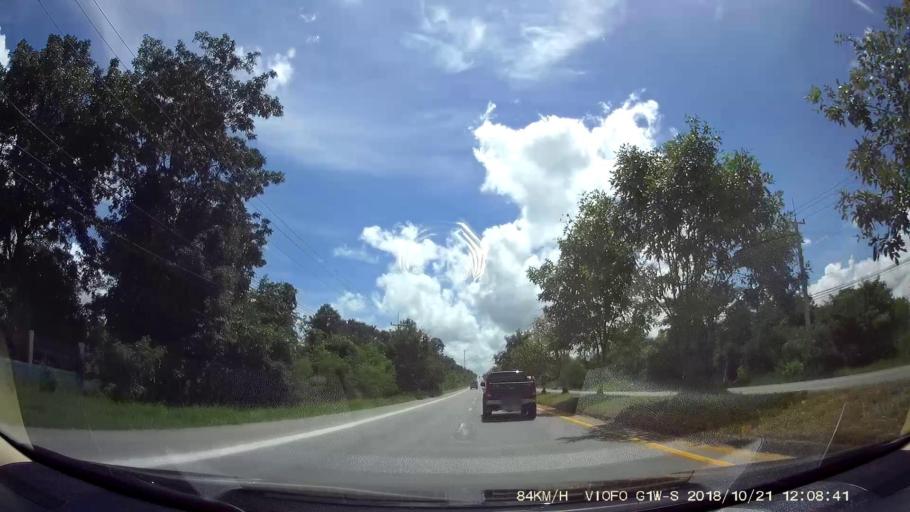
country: TH
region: Chaiyaphum
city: Chatturat
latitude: 15.4306
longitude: 101.8310
